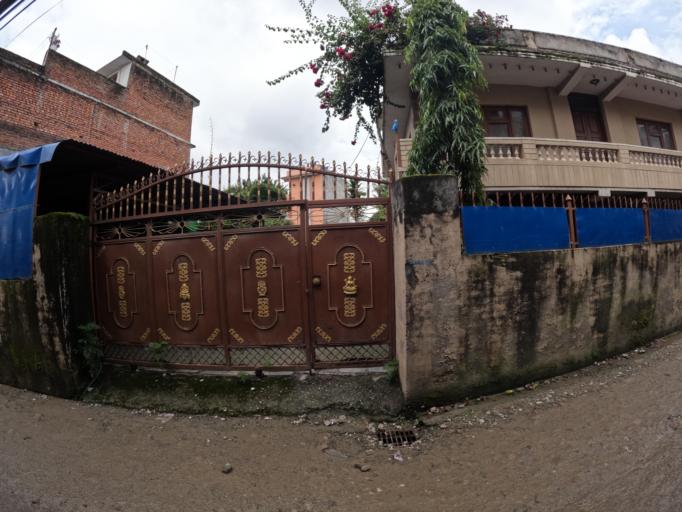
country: NP
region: Central Region
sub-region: Bagmati Zone
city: Kathmandu
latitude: 27.7469
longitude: 85.3200
